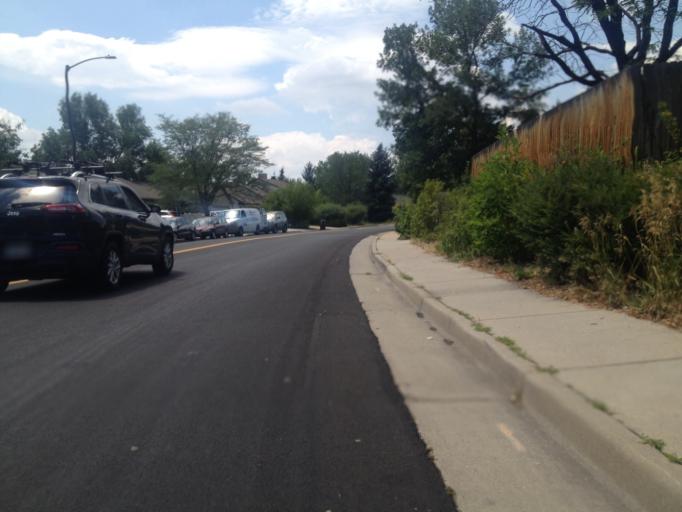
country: US
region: Colorado
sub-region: Boulder County
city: Louisville
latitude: 39.9691
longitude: -105.1519
